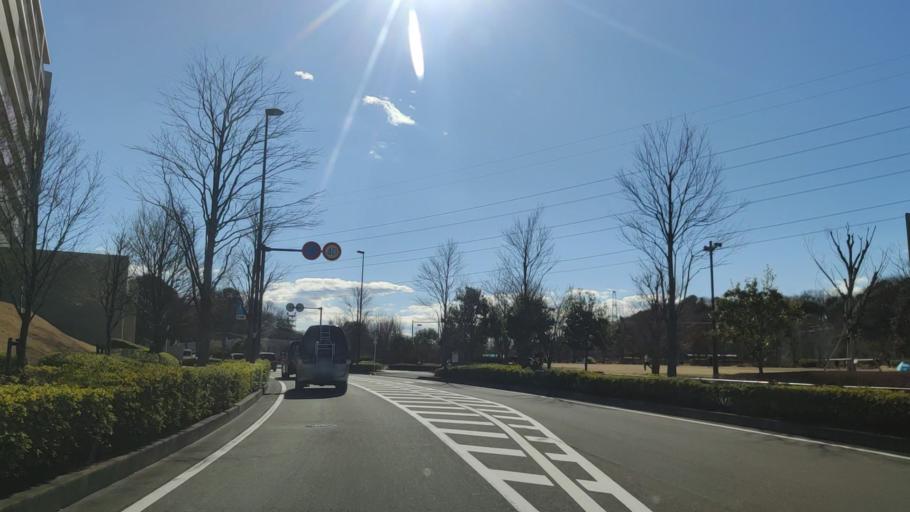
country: JP
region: Tokyo
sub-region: Machida-shi
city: Machida
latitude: 35.5197
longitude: 139.4969
